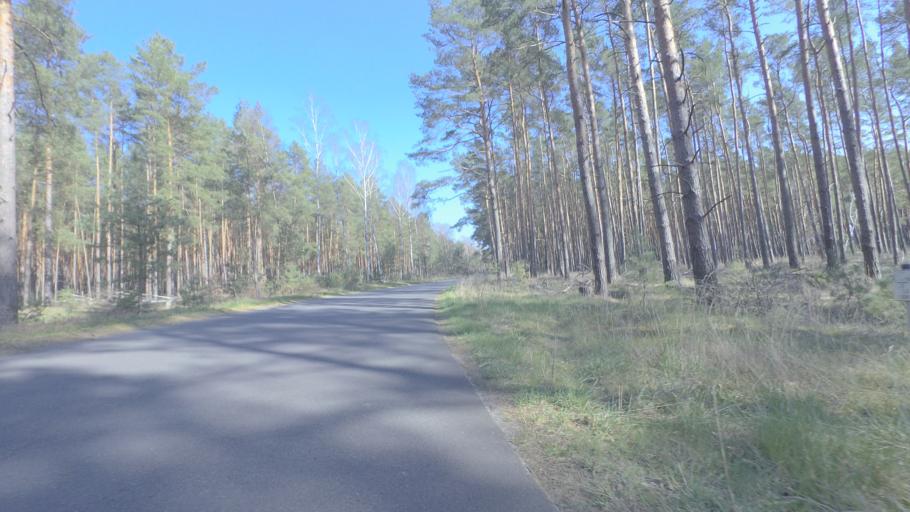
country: DE
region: Brandenburg
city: Munchehofe
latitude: 52.1635
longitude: 13.8036
